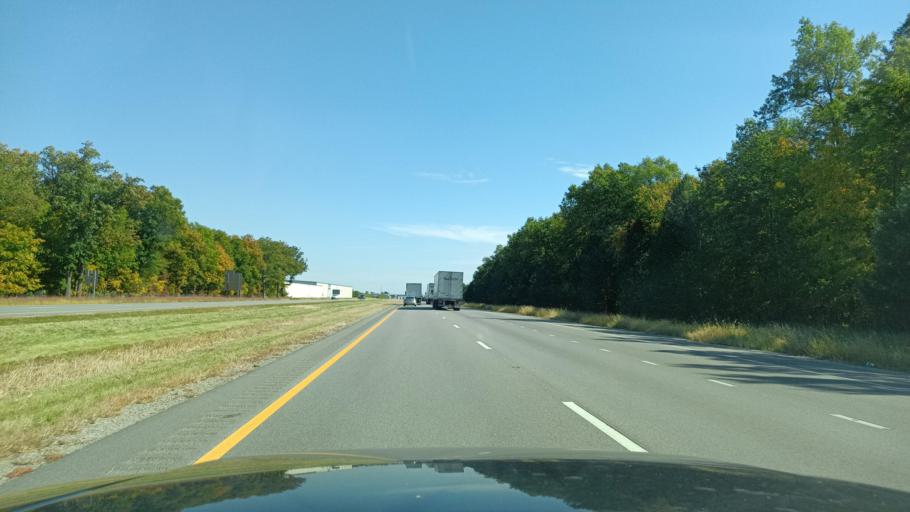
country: US
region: Ohio
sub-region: Defiance County
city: Defiance
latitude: 41.3081
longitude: -84.3548
